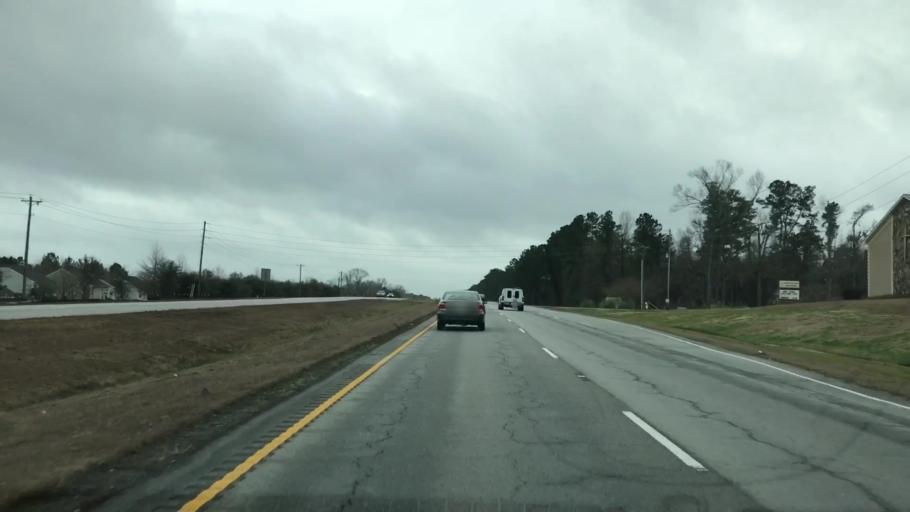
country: US
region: South Carolina
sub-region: Berkeley County
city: Moncks Corner
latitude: 33.1370
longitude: -80.0320
